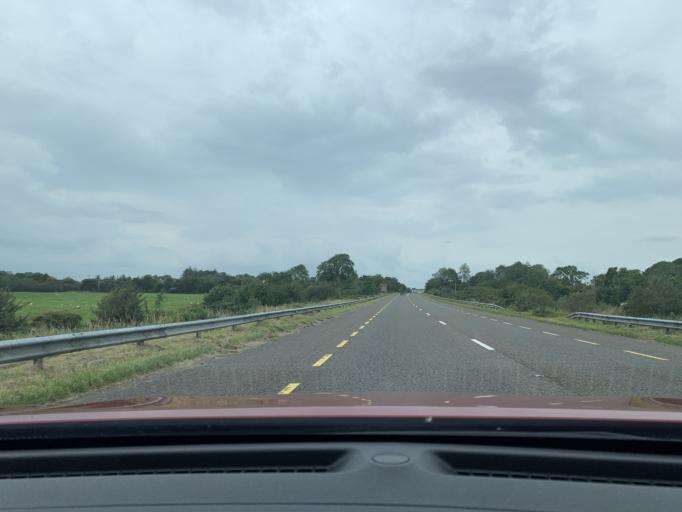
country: IE
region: Connaught
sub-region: Maigh Eo
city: Claremorris
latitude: 53.7744
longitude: -8.9530
